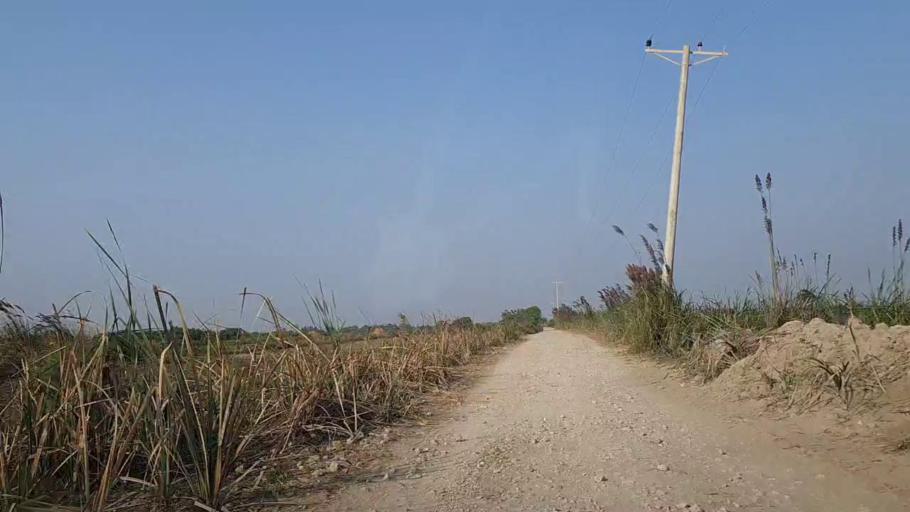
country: PK
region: Sindh
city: Mirpur Sakro
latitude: 24.6284
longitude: 67.7459
